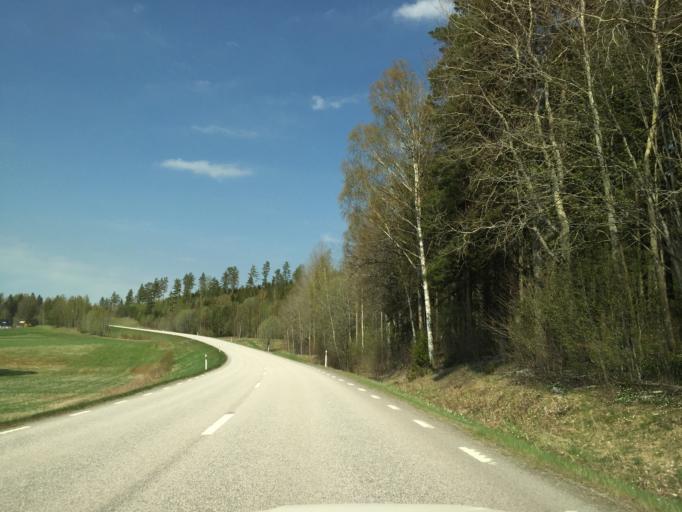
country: SE
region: Vaestra Goetaland
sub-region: Bengtsfors Kommun
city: Billingsfors
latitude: 58.9177
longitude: 12.2231
